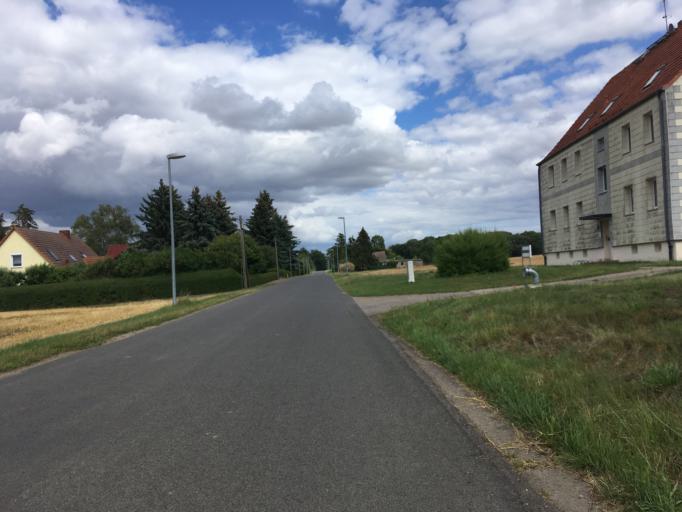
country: DE
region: Brandenburg
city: Gramzow
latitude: 53.2712
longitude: 14.0160
